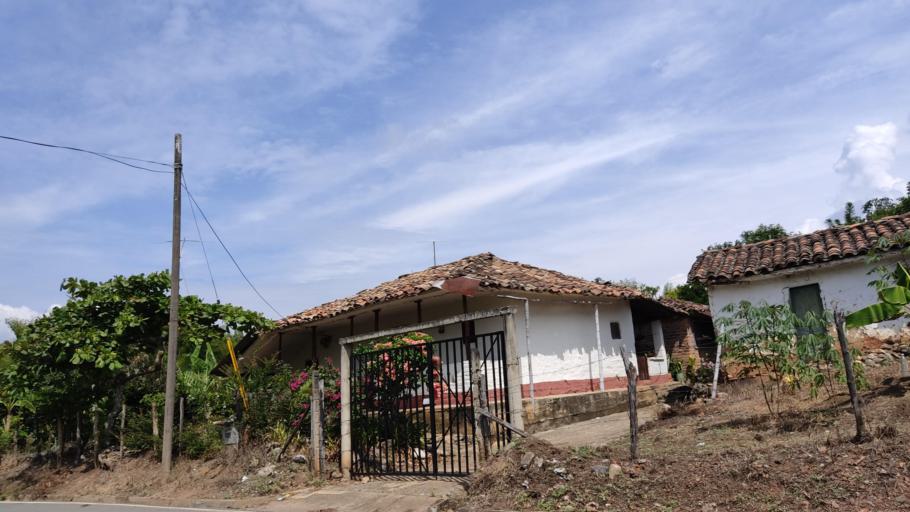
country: CO
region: Cauca
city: Buenos Aires
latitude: 3.1323
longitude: -76.5921
